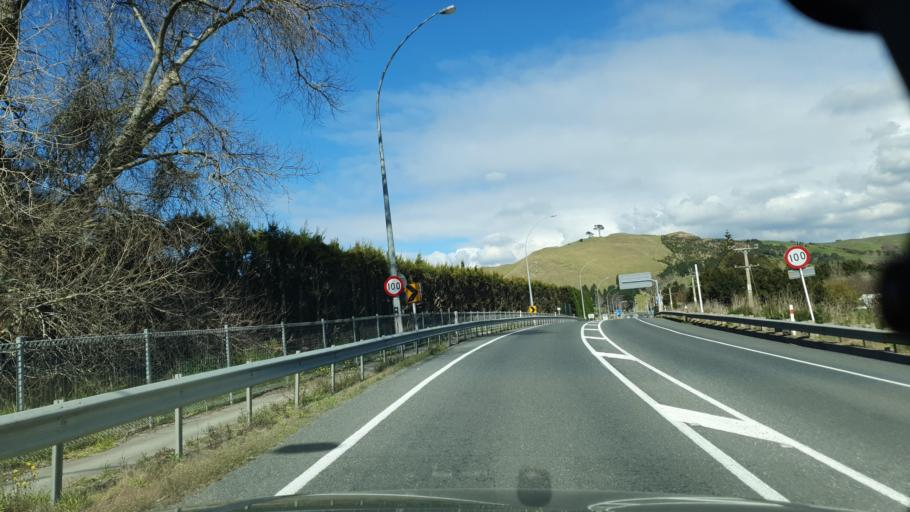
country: NZ
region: Bay of Plenty
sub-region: Tauranga City
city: Tauranga
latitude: -37.7172
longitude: 176.2843
